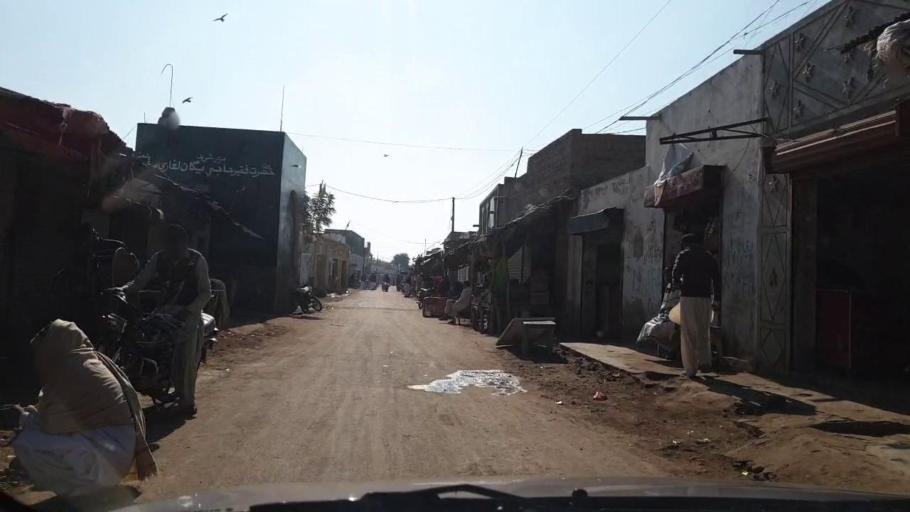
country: PK
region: Sindh
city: Sinjhoro
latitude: 25.9670
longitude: 68.7447
